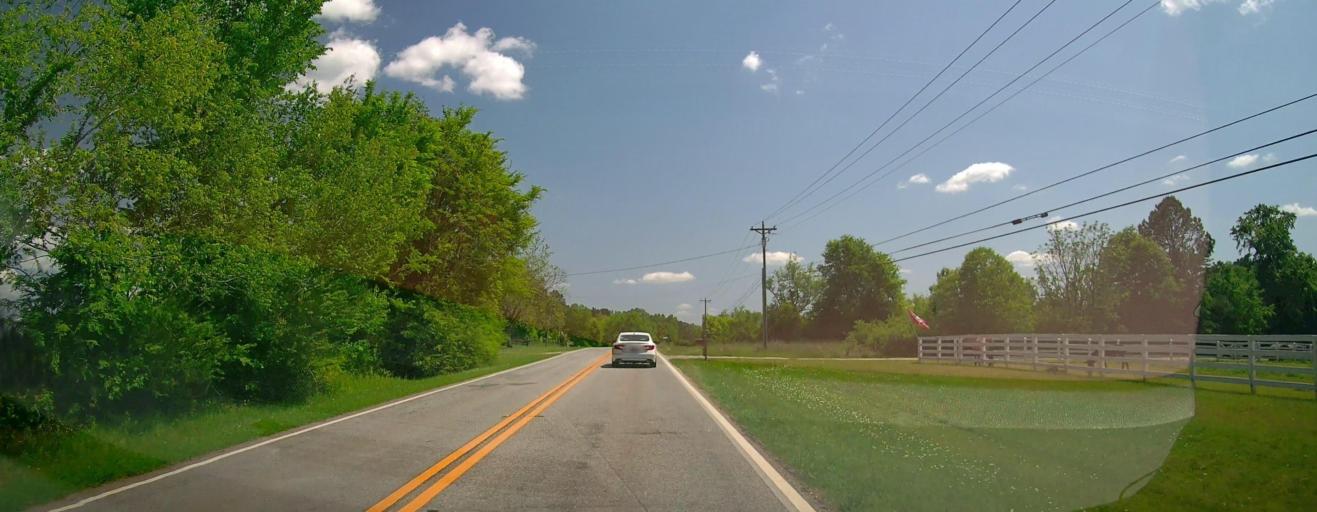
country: US
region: Georgia
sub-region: Putnam County
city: Eatonton
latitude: 33.2938
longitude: -83.3017
